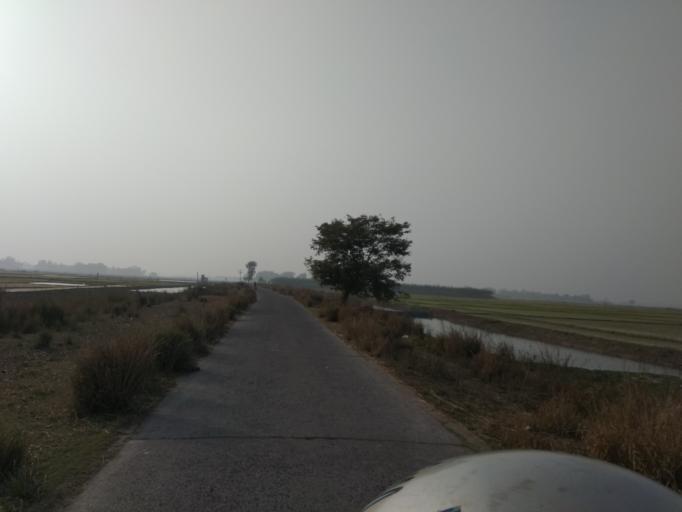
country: BD
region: Rajshahi
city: Ishurdi
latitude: 24.4962
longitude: 89.1879
